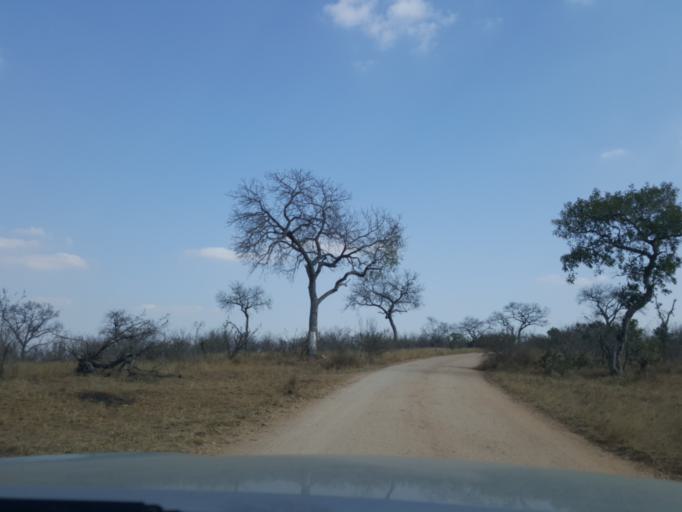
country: ZA
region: Mpumalanga
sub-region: Ehlanzeni District
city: Komatipoort
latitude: -25.2928
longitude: 31.7632
